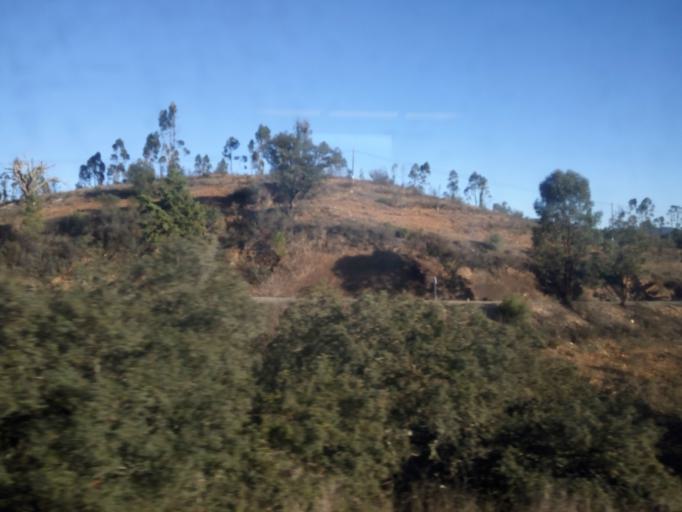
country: PT
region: Beja
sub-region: Odemira
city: Odemira
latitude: 37.5229
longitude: -8.4755
